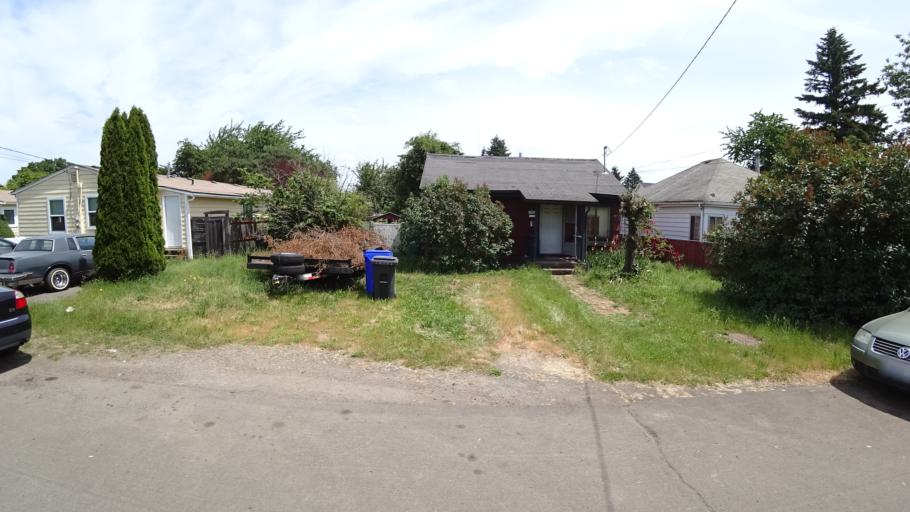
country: US
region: Oregon
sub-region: Multnomah County
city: Lents
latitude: 45.4718
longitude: -122.5981
